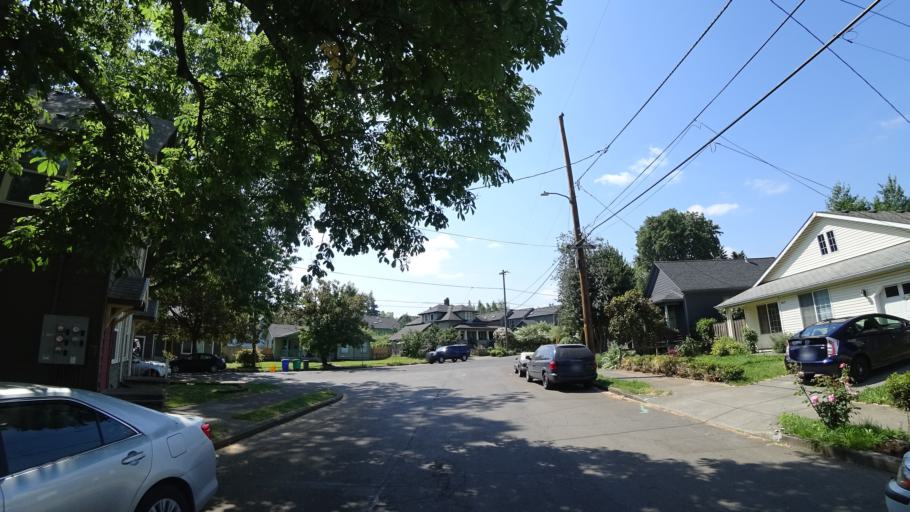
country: US
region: Oregon
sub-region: Multnomah County
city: Portland
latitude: 45.5738
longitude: -122.6557
